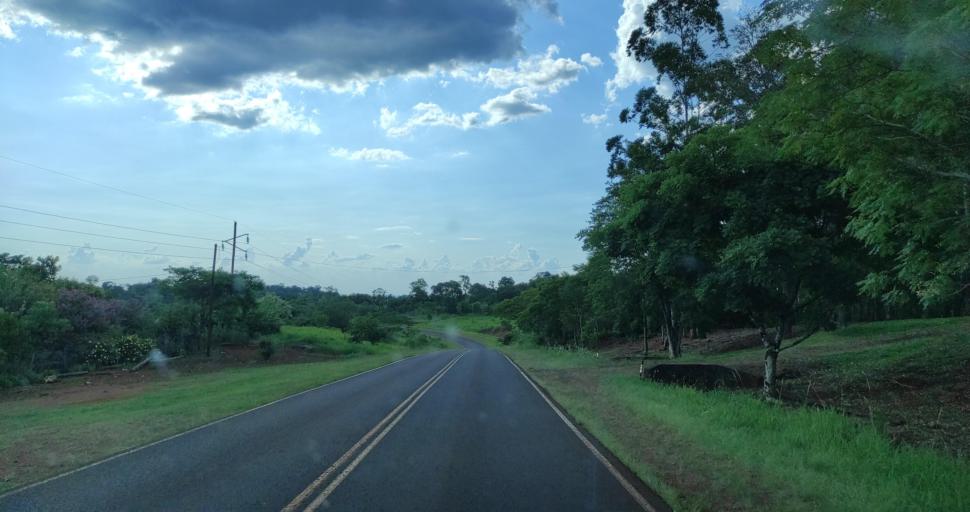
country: AR
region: Misiones
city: San Vicente
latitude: -26.3376
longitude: -54.1713
